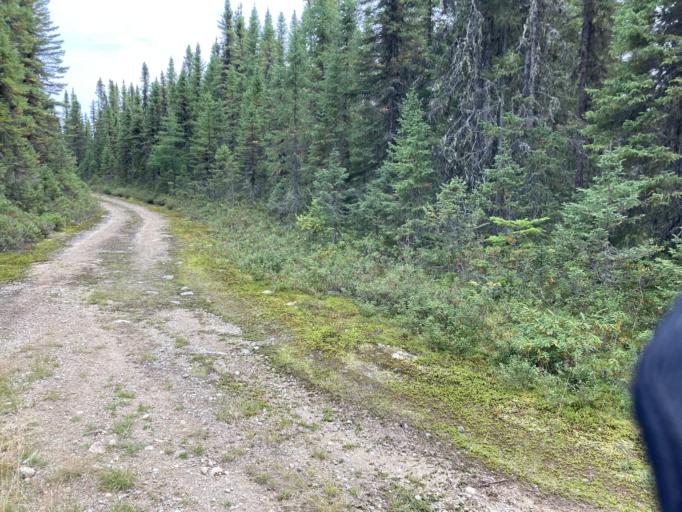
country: CA
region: Quebec
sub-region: Capitale-Nationale
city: Baie-Saint-Paul
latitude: 47.7188
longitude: -70.9417
